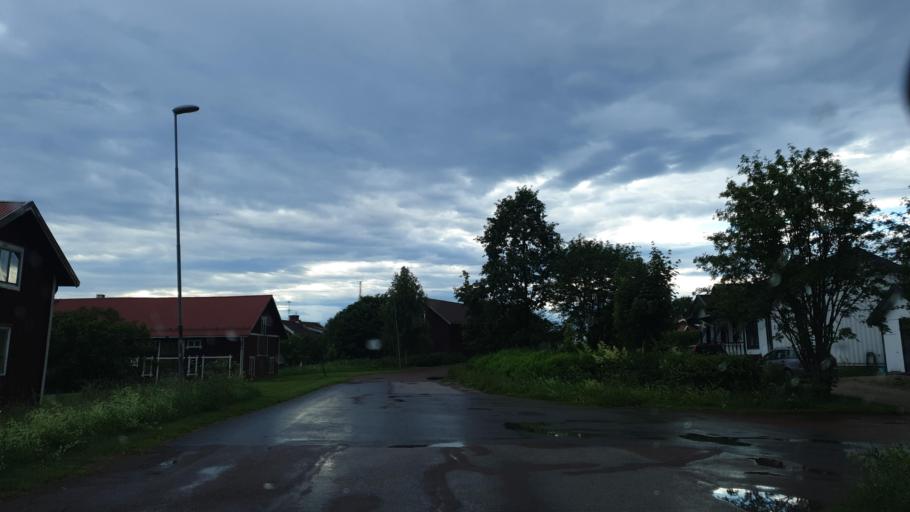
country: SE
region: Dalarna
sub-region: Mora Kommun
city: Mora
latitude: 61.0009
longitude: 14.5853
